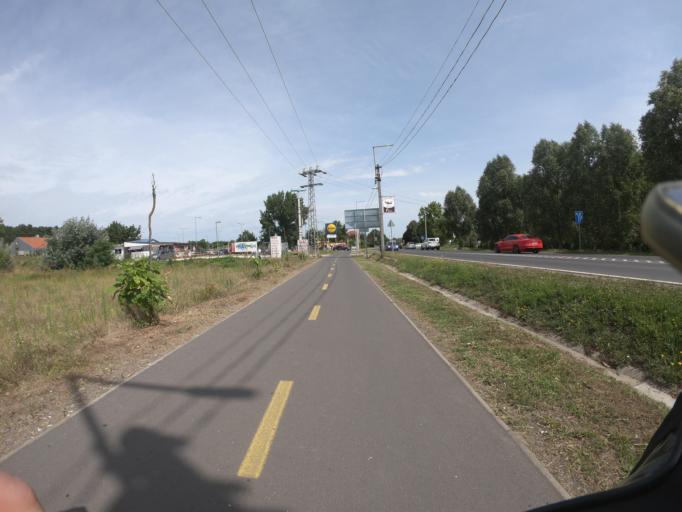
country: HU
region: Jasz-Nagykun-Szolnok
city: Tiszafured
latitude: 47.6227
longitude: 20.7475
